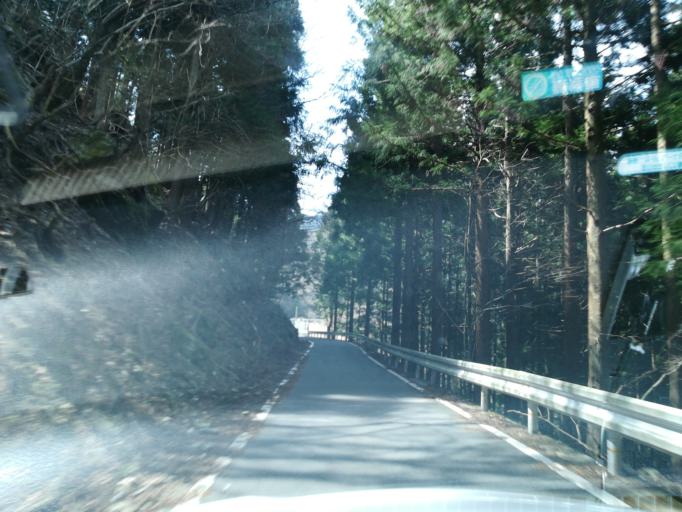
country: JP
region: Tokushima
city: Wakimachi
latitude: 33.8885
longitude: 134.0588
